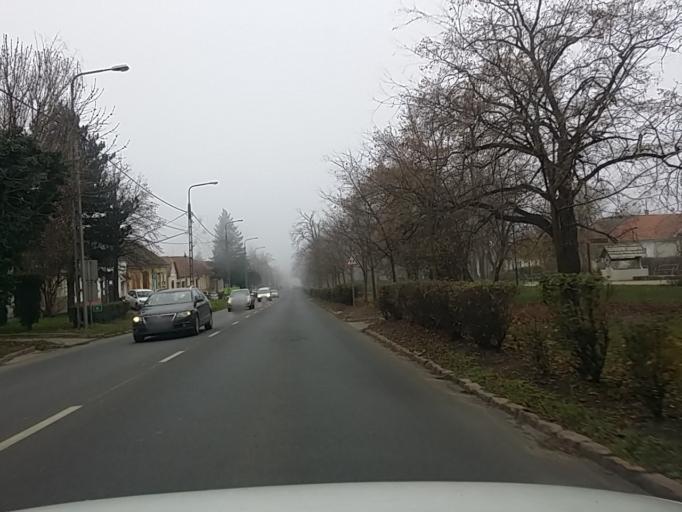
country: HU
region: Pest
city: Budakeszi
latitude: 47.5159
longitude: 18.9349
